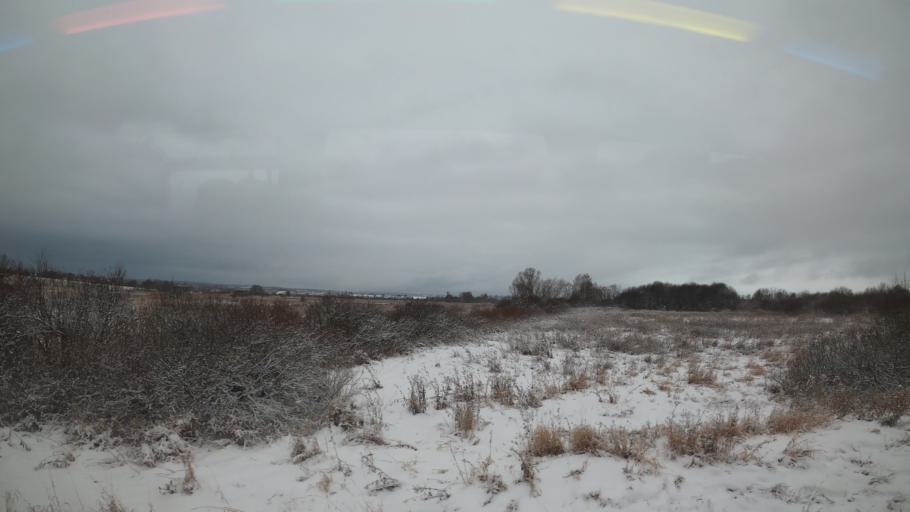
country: RU
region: Jaroslavl
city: Pereslavl'-Zalesskiy
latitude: 56.7179
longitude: 38.9085
